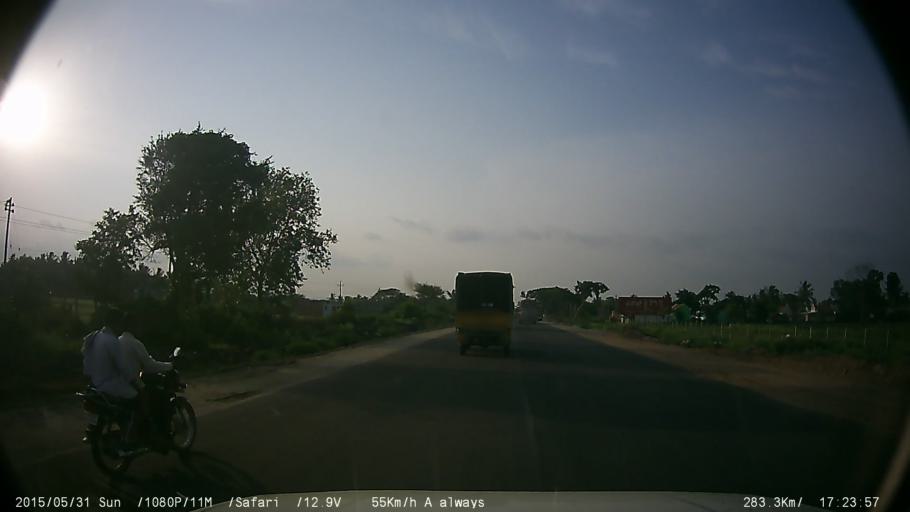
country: IN
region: Karnataka
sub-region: Chamrajnagar
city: Gundlupet
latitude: 11.8447
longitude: 76.6728
